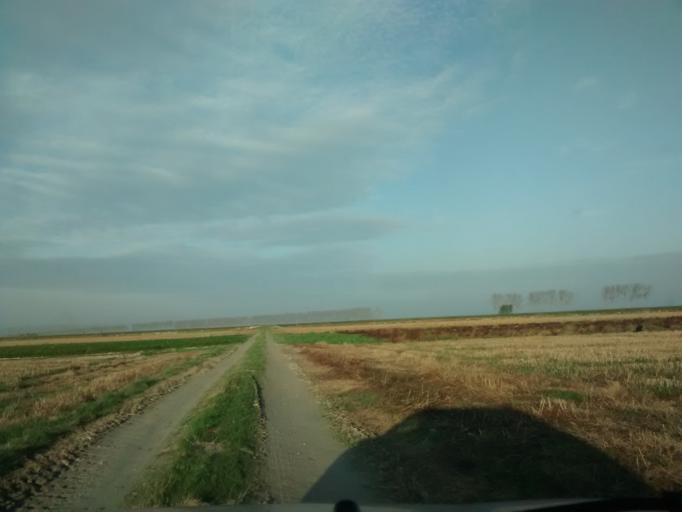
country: FR
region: Brittany
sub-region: Departement d'Ille-et-Vilaine
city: Roz-sur-Couesnon
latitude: 48.6140
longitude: -1.5589
